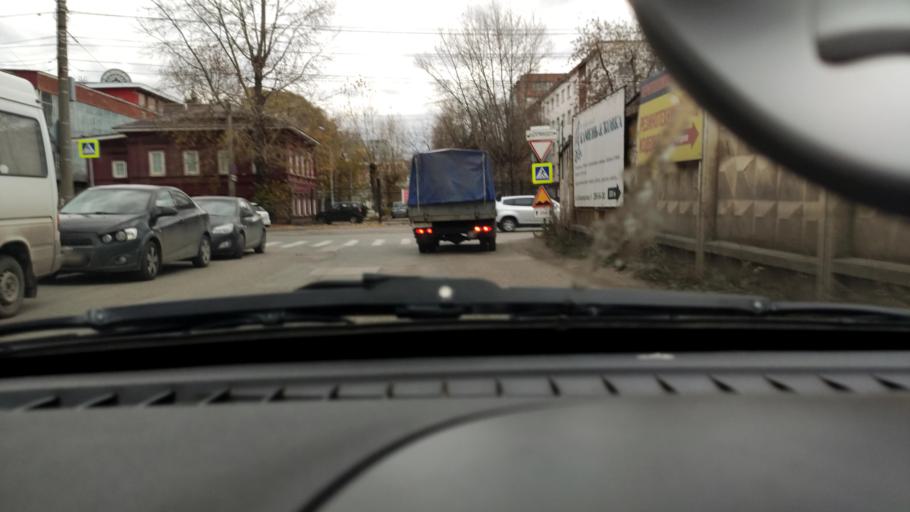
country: RU
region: Perm
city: Perm
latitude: 58.0096
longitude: 56.1868
